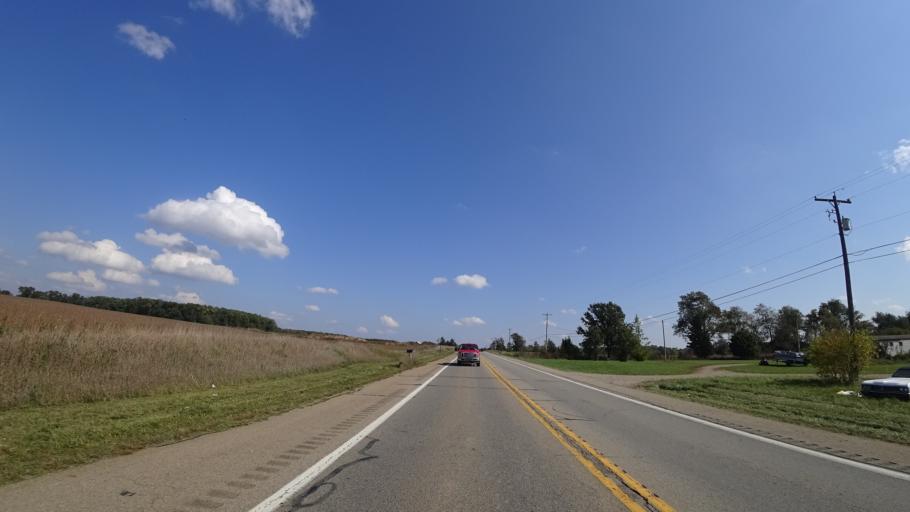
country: US
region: Michigan
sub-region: Calhoun County
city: Homer
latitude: 42.1617
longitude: -84.7404
